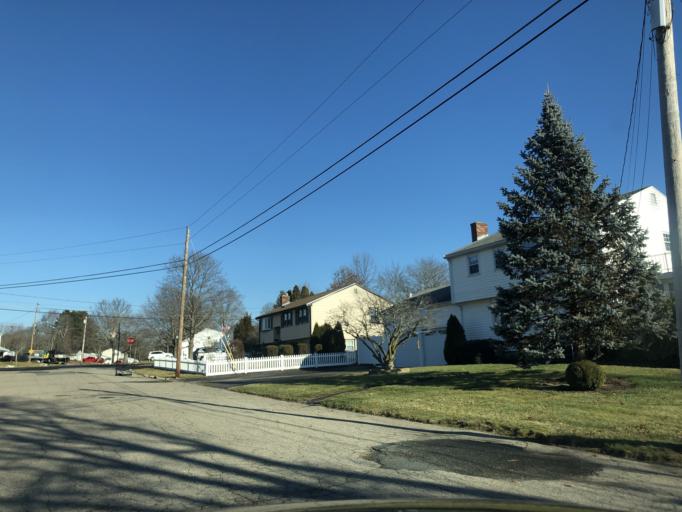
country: US
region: Massachusetts
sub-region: Plymouth County
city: Brockton
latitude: 42.1019
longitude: -71.0017
